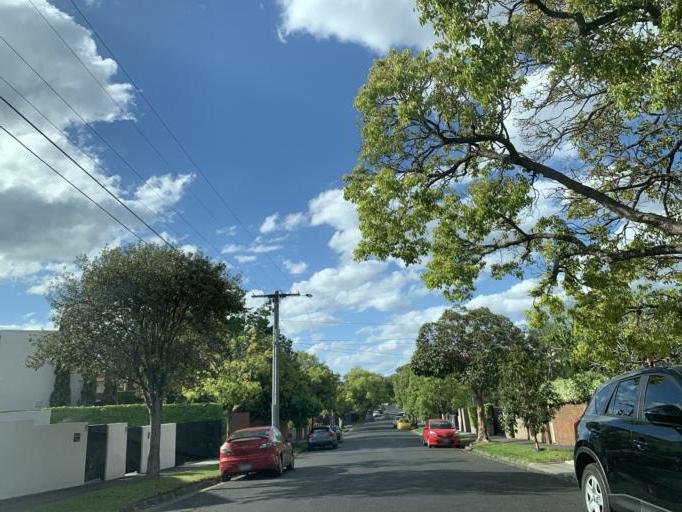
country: AU
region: Victoria
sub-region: Bayside
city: North Brighton
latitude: -37.9185
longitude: 145.0035
